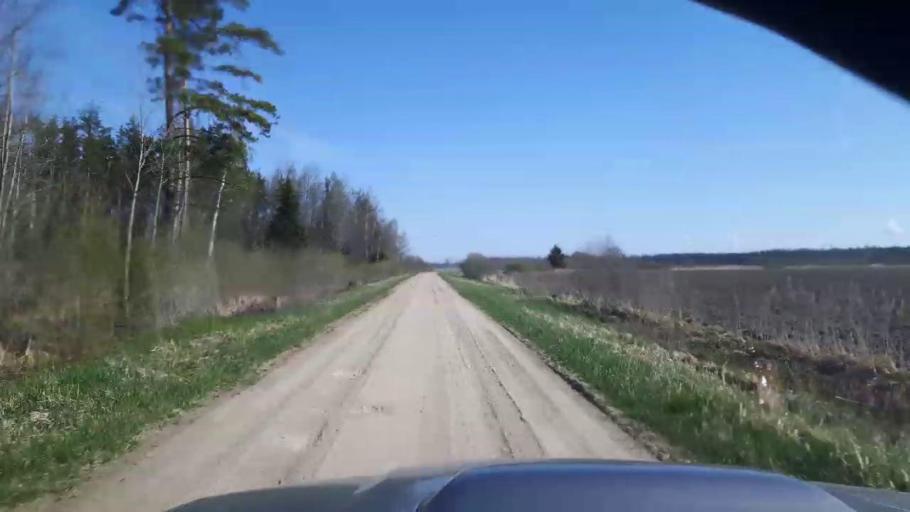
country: EE
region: Paernumaa
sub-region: Vaendra vald (alev)
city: Vandra
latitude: 58.5272
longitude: 24.9616
